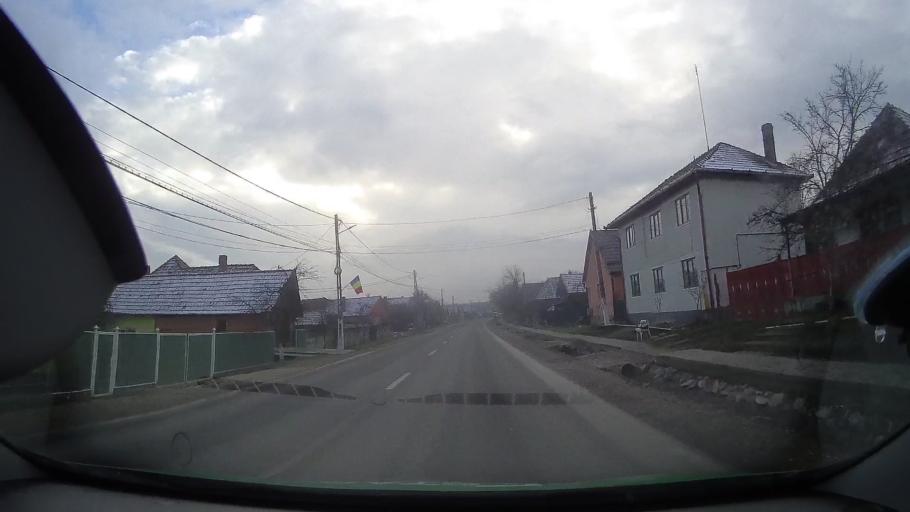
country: RO
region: Mures
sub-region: Comuna Cucerdea
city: Cucerdea
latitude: 46.4002
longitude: 24.2613
